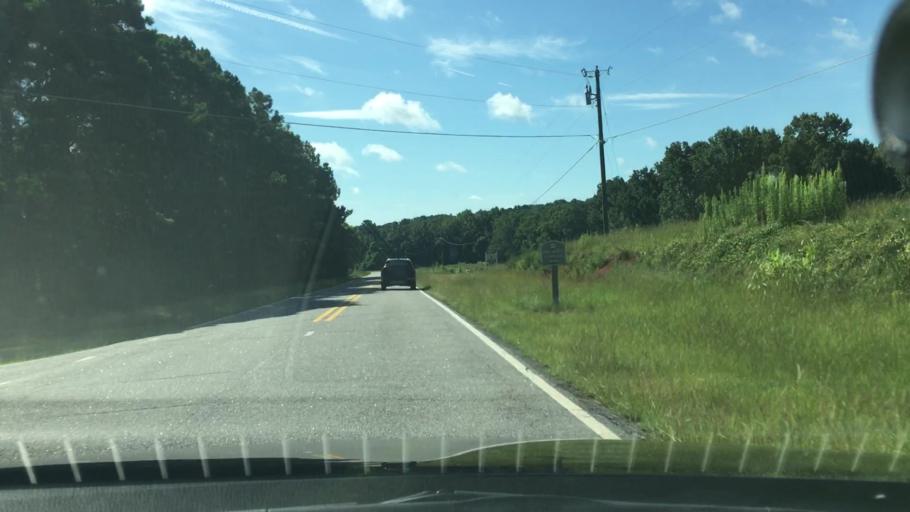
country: US
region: Georgia
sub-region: Putnam County
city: Jefferson
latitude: 33.3935
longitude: -83.2672
